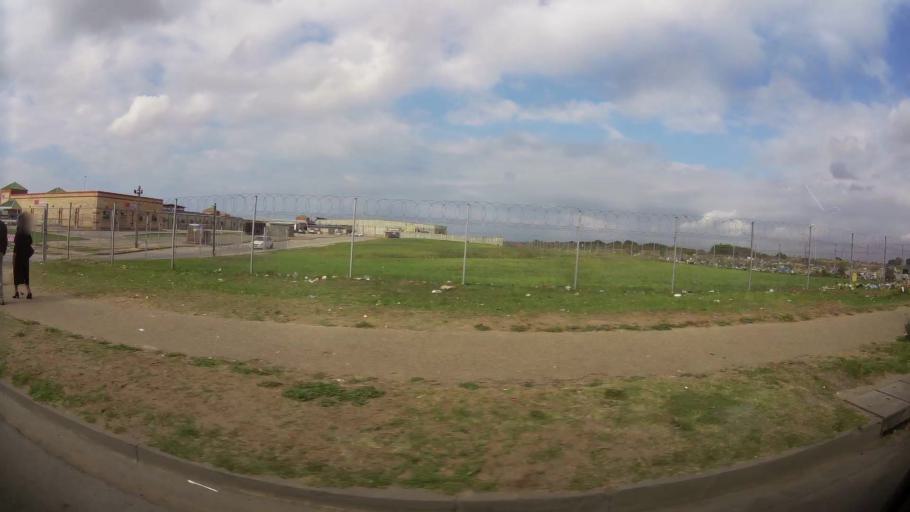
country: ZA
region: Eastern Cape
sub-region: Nelson Mandela Bay Metropolitan Municipality
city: Port Elizabeth
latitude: -33.8107
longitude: 25.5928
